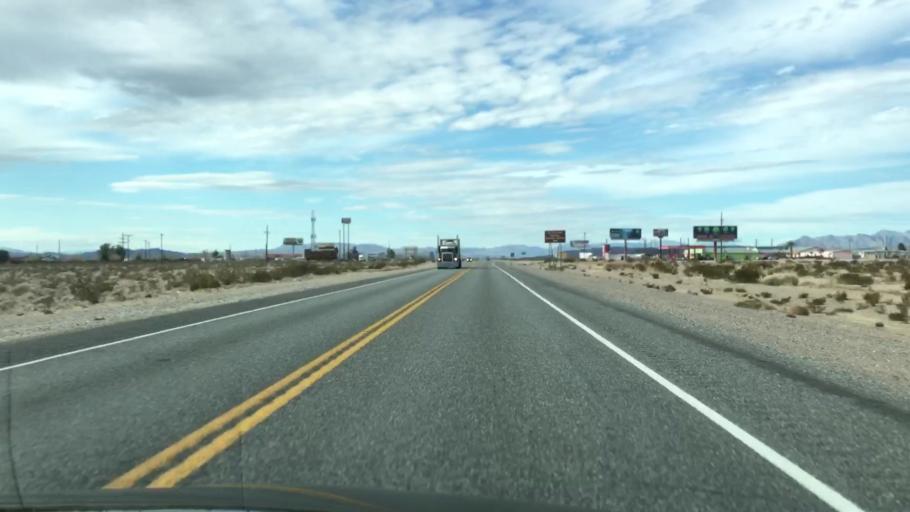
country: US
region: Nevada
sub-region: Nye County
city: Beatty
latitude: 36.6417
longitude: -116.3918
